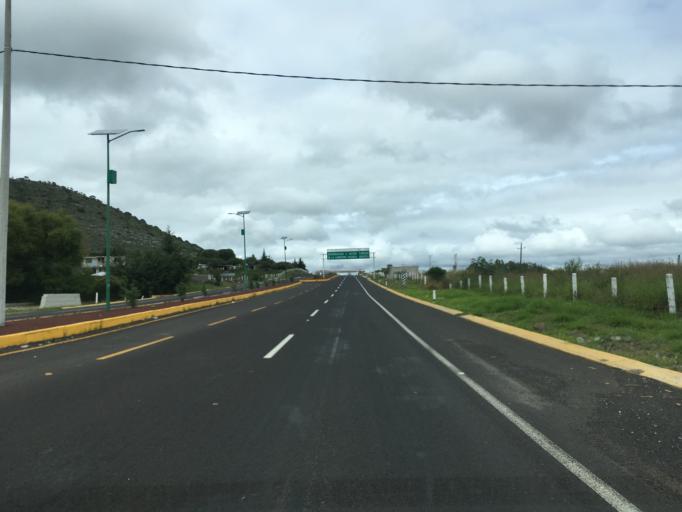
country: MX
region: Hidalgo
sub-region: Atotonilco el Grande
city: La Estancia
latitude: 20.3310
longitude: -98.7013
